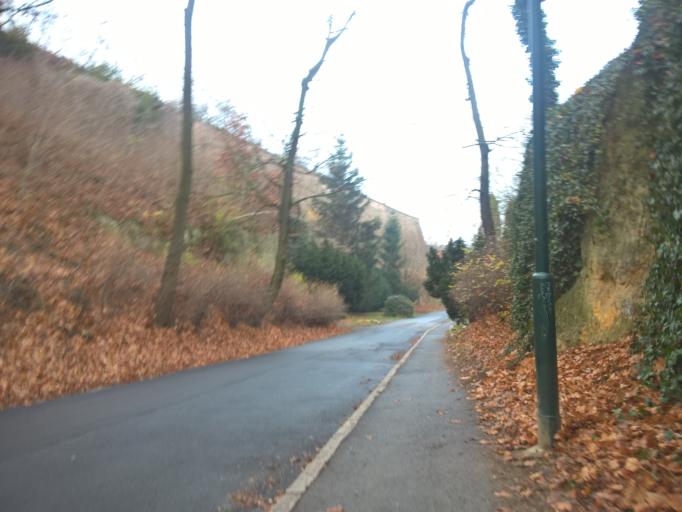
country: CZ
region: Praha
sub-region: Praha 1
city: Mala Strana
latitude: 50.0848
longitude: 14.3885
